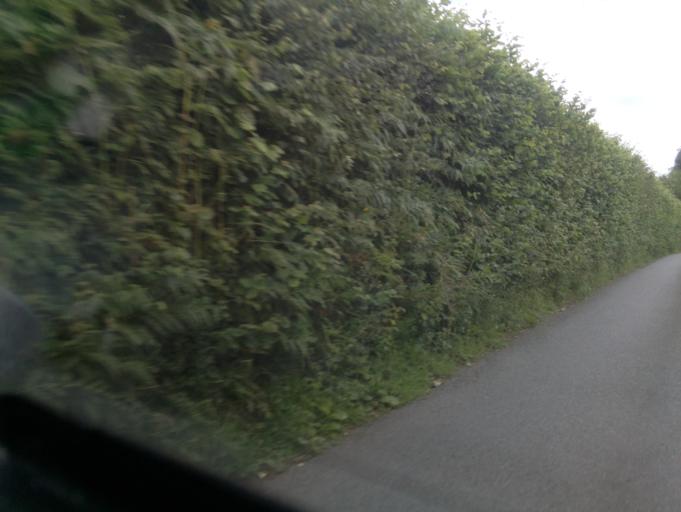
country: GB
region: England
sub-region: Gloucestershire
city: Cinderford
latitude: 51.8144
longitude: -2.4831
